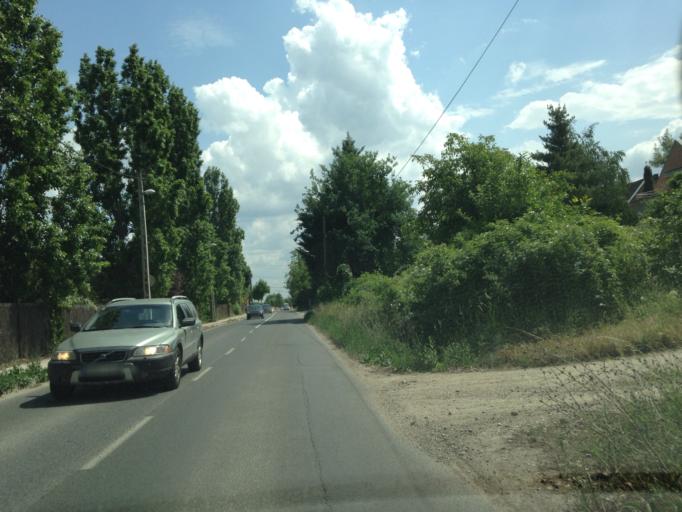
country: HU
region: Pest
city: Szentendre
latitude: 47.6790
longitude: 19.0656
